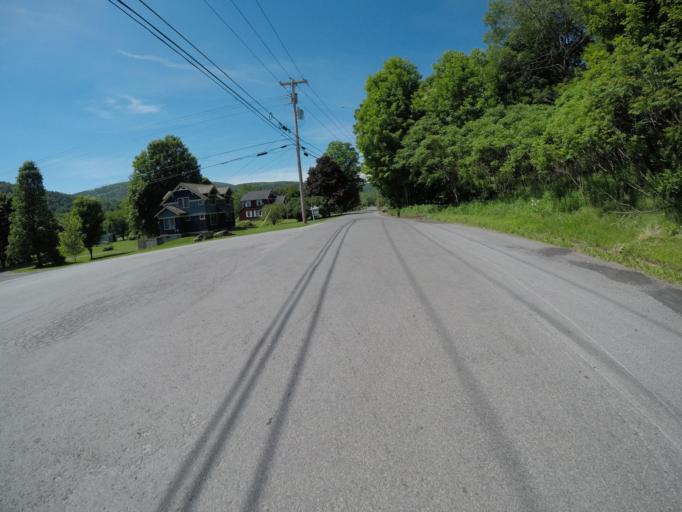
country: US
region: New York
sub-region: Delaware County
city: Delhi
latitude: 42.2658
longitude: -74.9243
